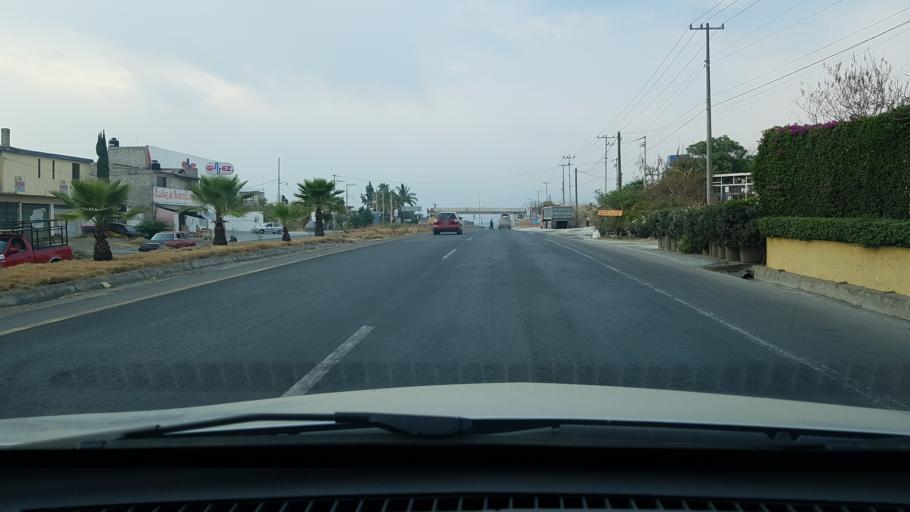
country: MX
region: Morelos
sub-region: Yecapixtla
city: Juan Morales
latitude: 18.8114
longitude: -98.9161
